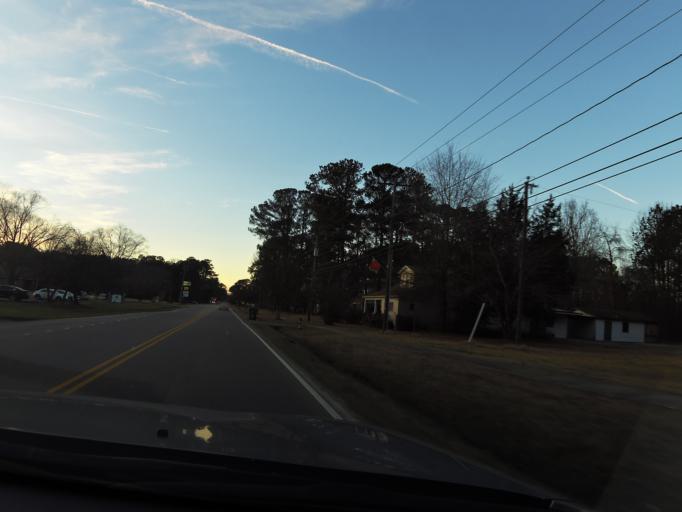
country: US
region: Virginia
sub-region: Southampton County
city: Courtland
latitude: 36.7082
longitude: -77.0542
